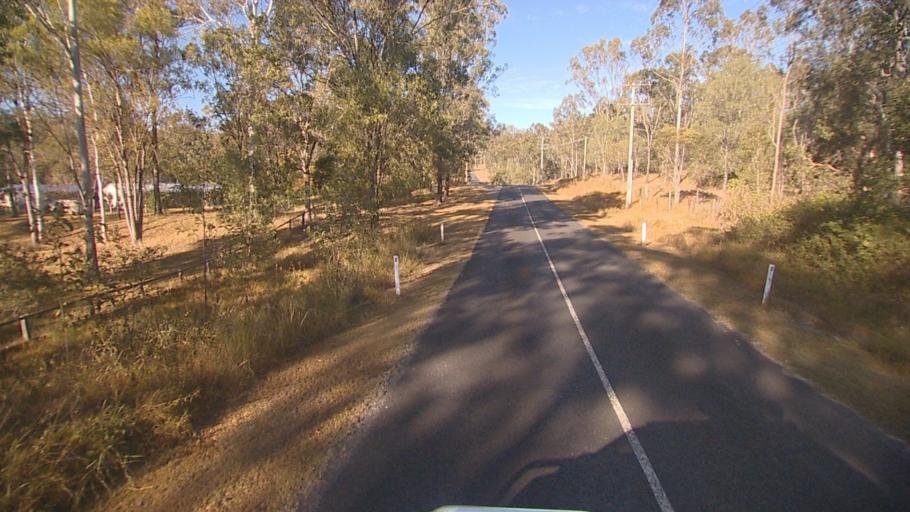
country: AU
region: Queensland
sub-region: Logan
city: Cedar Vale
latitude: -27.8425
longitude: 153.0827
